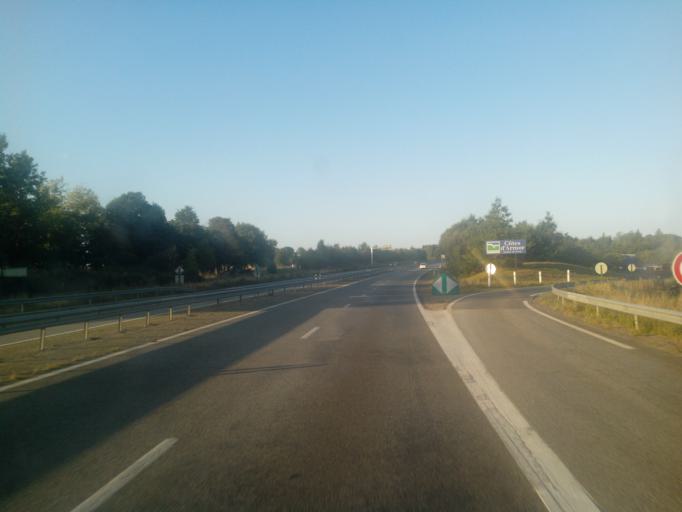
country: FR
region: Brittany
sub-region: Departement du Morbihan
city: Saint-Gonnery
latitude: 48.1365
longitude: -2.7959
